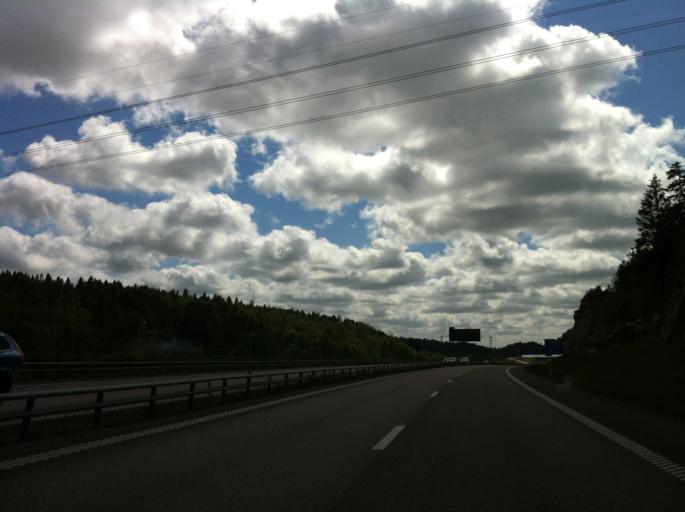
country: SE
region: Vaestra Goetaland
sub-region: Ale Kommun
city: Alvangen
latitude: 57.9462
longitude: 12.0985
